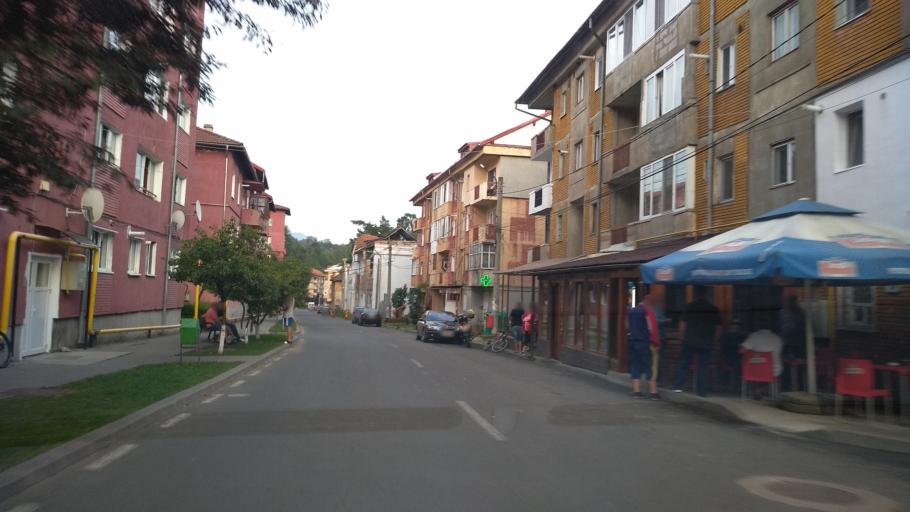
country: RO
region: Hunedoara
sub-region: Comuna Aninoasa
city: Aninoasa
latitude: 45.4089
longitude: 23.3143
